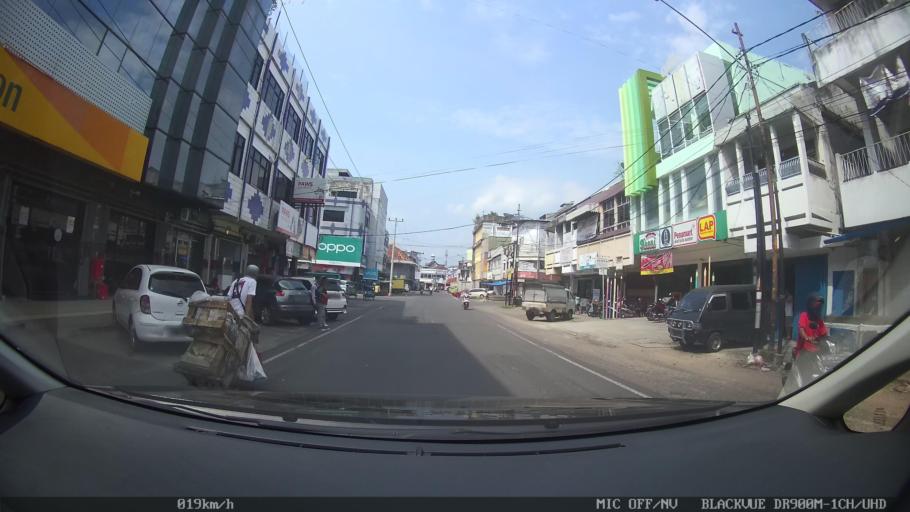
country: ID
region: Lampung
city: Bandarlampung
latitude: -5.4476
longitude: 105.2645
